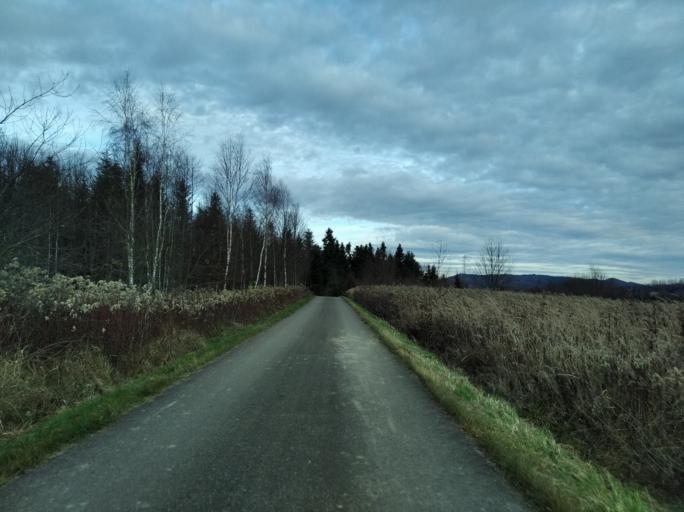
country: PL
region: Subcarpathian Voivodeship
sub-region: Powiat brzozowski
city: Domaradz
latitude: 49.7818
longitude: 21.9163
